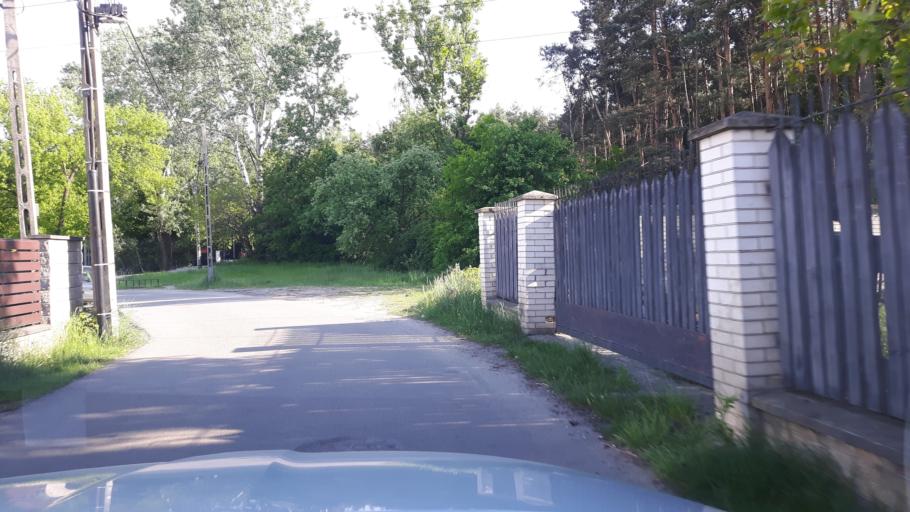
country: PL
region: Masovian Voivodeship
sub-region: Warszawa
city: Praga Poludnie
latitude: 52.2527
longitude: 21.1210
